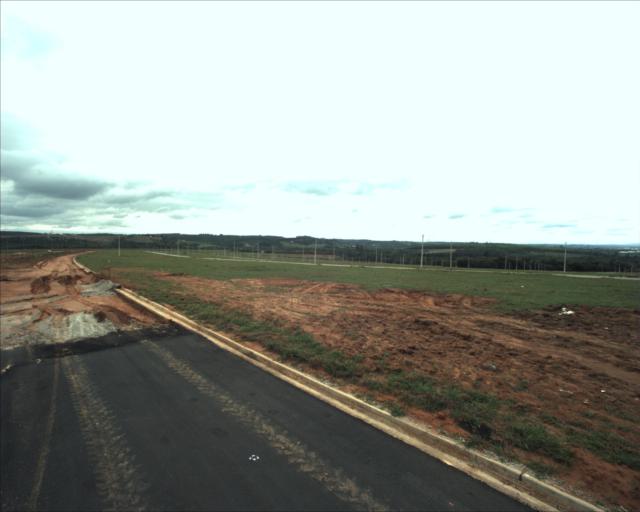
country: BR
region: Sao Paulo
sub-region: Sorocaba
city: Sorocaba
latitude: -23.4216
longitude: -47.4690
